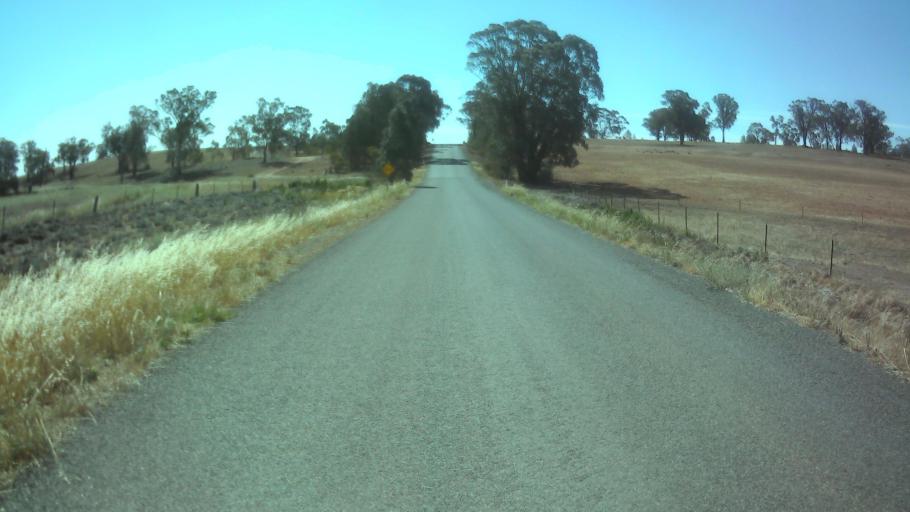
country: AU
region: New South Wales
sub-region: Weddin
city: Grenfell
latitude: -33.7588
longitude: 147.8580
